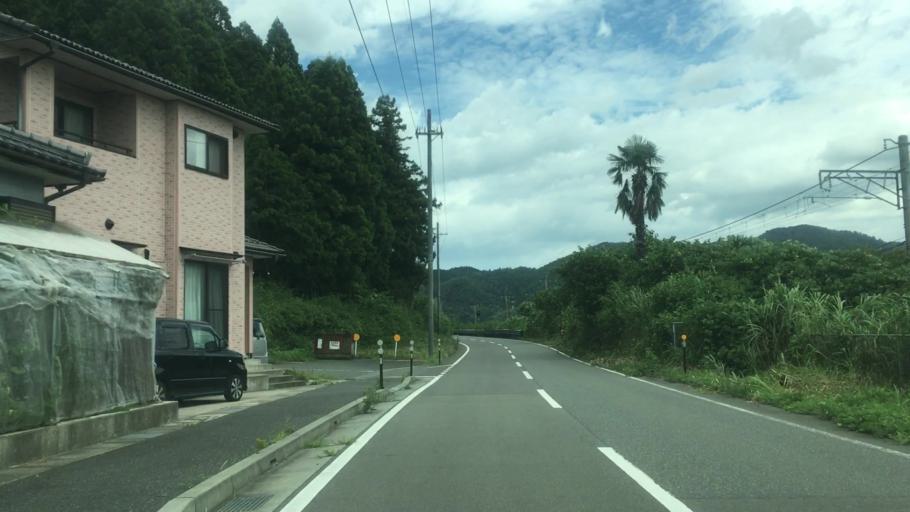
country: JP
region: Hyogo
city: Toyooka
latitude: 35.5714
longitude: 134.8045
